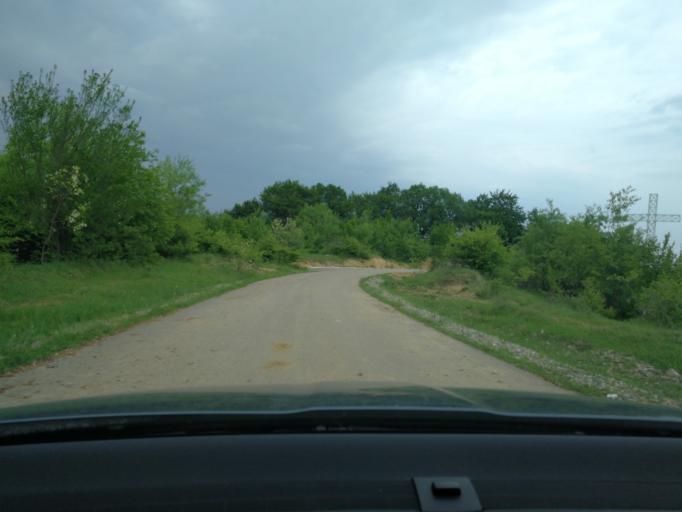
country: RO
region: Prahova
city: Cornu de Sus
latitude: 45.1739
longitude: 25.7059
